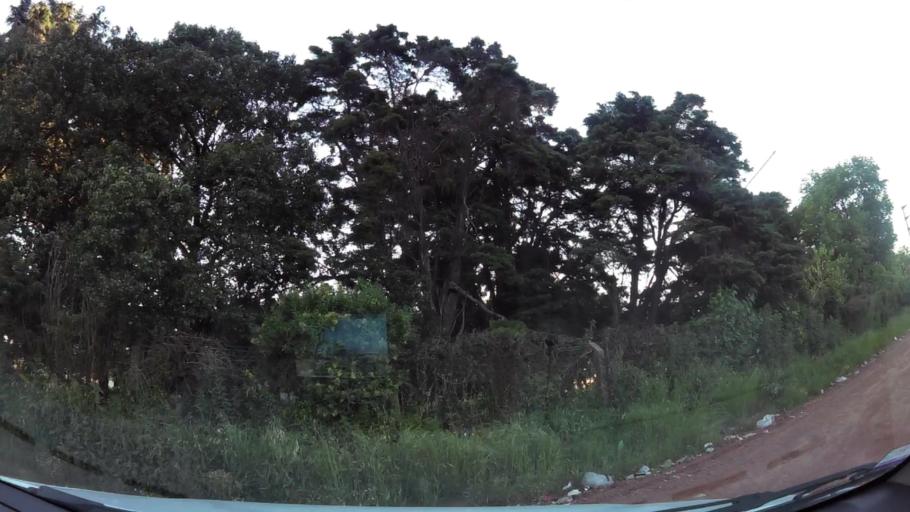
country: AR
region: Buenos Aires
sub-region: Partido de Moron
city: Moron
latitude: -34.7218
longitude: -58.6165
